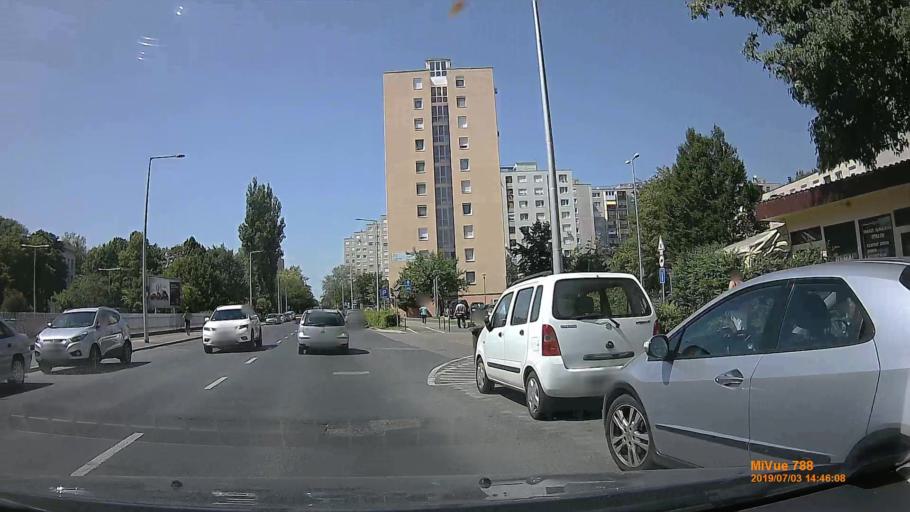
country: HU
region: Gyor-Moson-Sopron
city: Gyor
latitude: 47.6730
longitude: 17.6505
